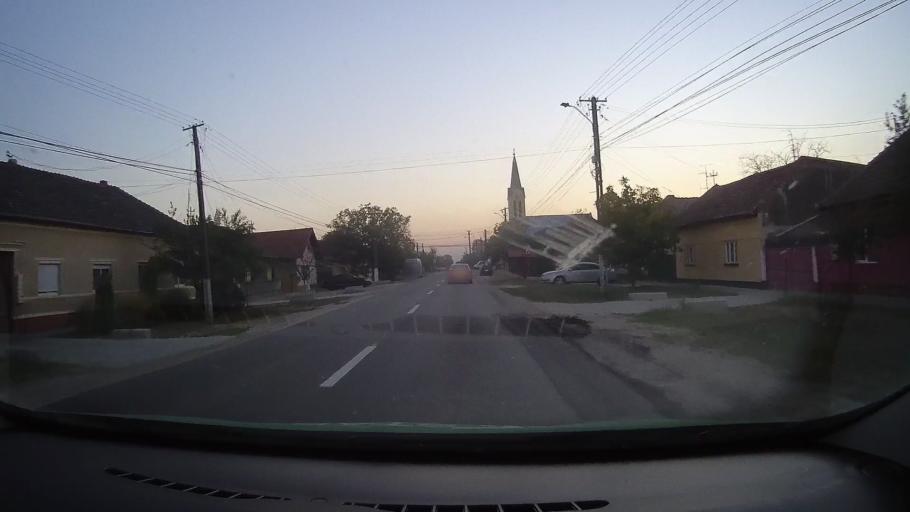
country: RO
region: Arad
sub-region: Comuna Zimandu Nou
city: Zimandu Nou
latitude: 46.2814
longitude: 21.3995
